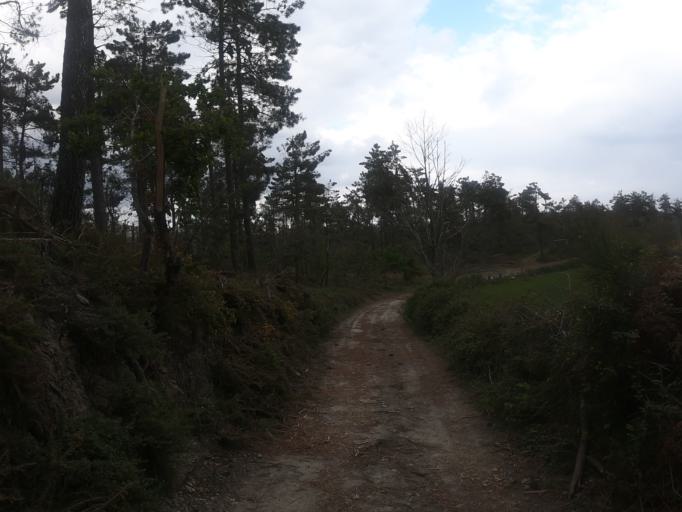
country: PT
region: Vila Real
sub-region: Mondim de Basto
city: Mondim de Basto
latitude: 41.3098
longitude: -7.8815
